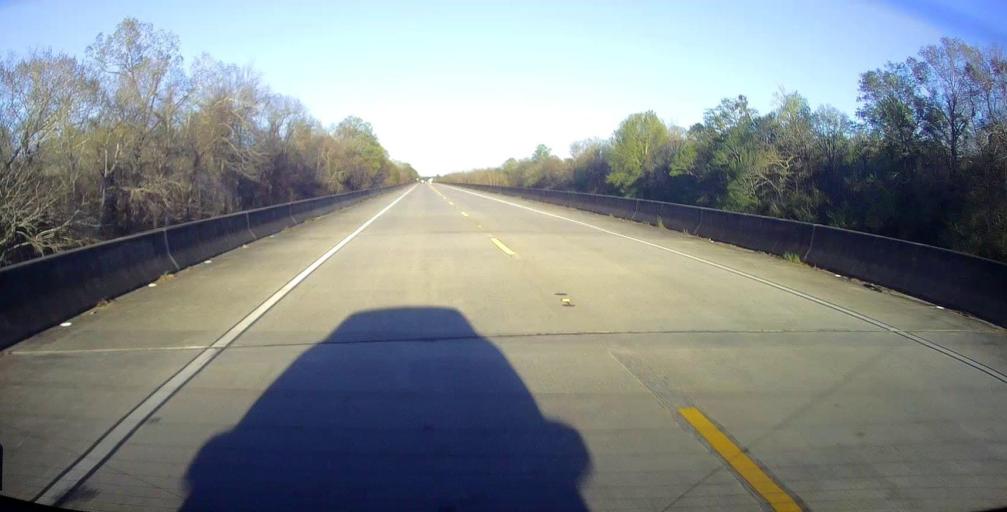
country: US
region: Georgia
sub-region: Wilcox County
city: Abbeville
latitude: 31.9959
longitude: -83.2839
